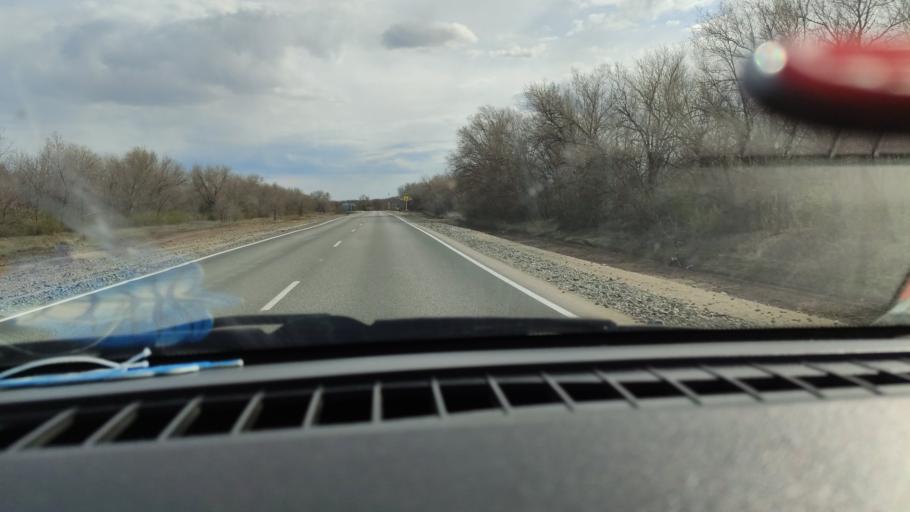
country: RU
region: Saratov
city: Krasnoarmeysk
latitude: 51.1194
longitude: 45.9561
